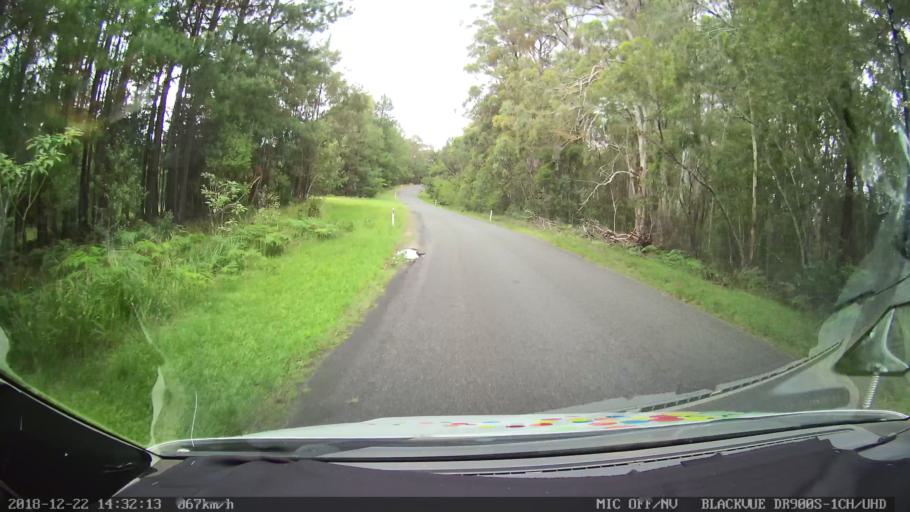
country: AU
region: New South Wales
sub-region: Bellingen
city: Dorrigo
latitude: -30.1016
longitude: 152.6273
